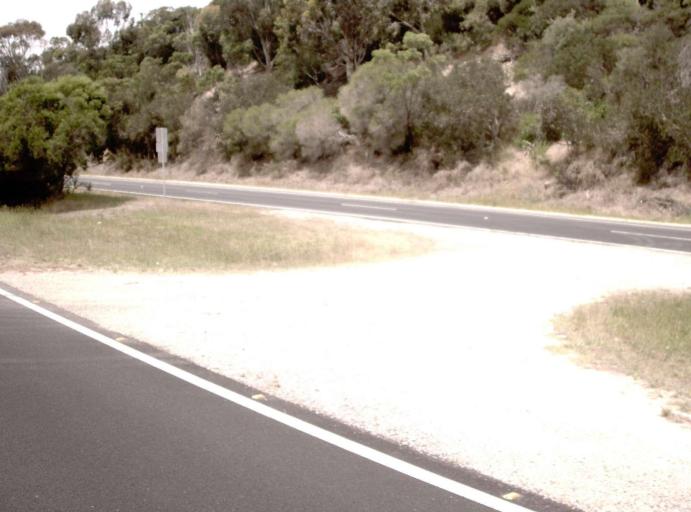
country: AU
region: Victoria
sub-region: Mornington Peninsula
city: McCrae
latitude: -38.3477
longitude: 144.9399
